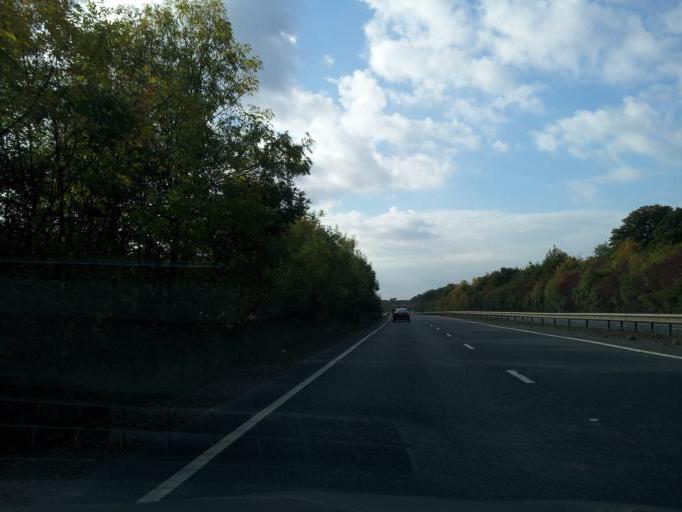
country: GB
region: England
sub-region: Northamptonshire
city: Blisworth
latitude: 52.1942
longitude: -0.9431
